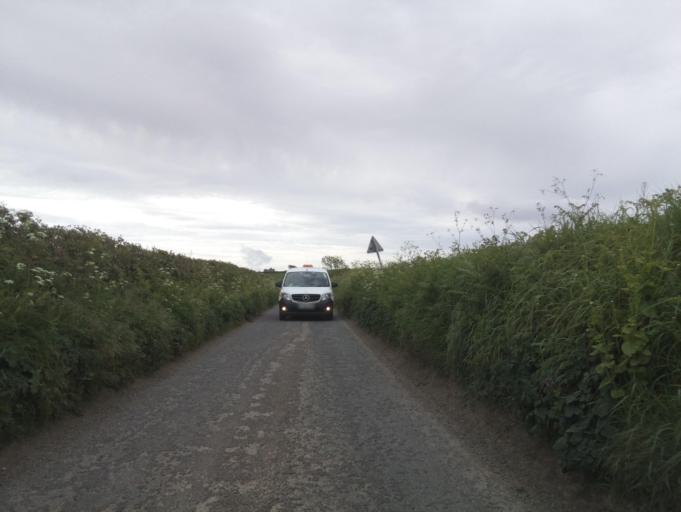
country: GB
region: England
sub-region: Devon
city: Dartmouth
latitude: 50.3234
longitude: -3.6384
